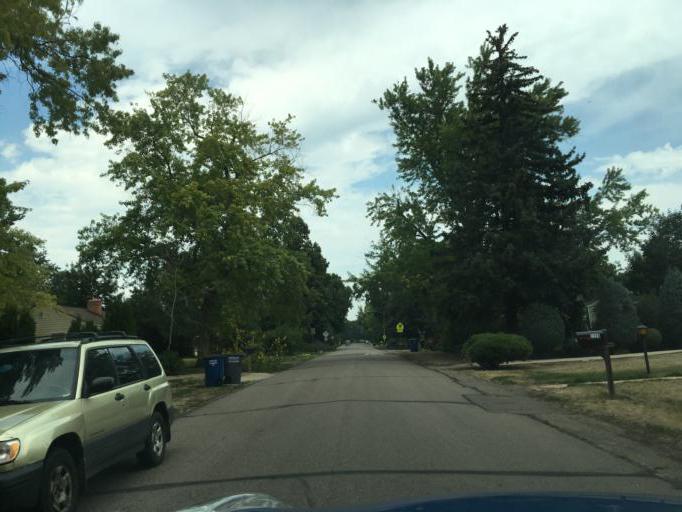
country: US
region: Colorado
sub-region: Jefferson County
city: Wheat Ridge
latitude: 39.7499
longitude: -105.0950
